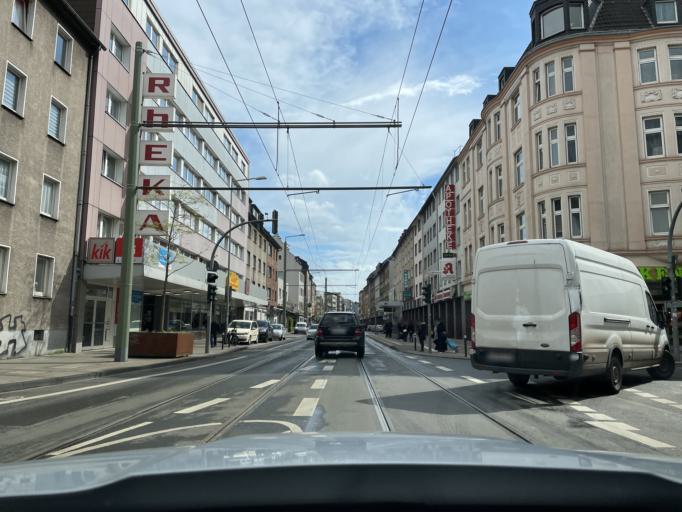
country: DE
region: North Rhine-Westphalia
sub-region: Regierungsbezirk Dusseldorf
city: Hochfeld
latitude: 51.4219
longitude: 6.7543
